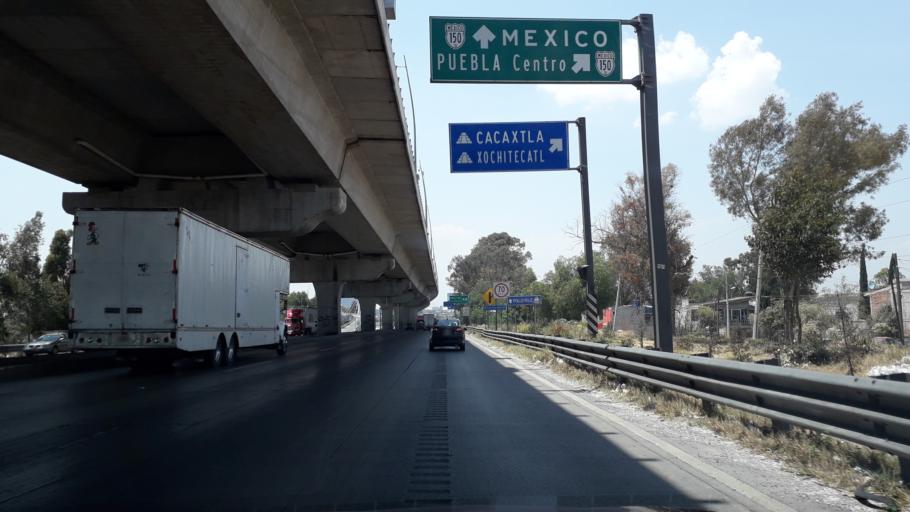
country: MX
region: Puebla
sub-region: Cuautlancingo
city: Sanctorum
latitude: 19.0944
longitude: -98.2255
